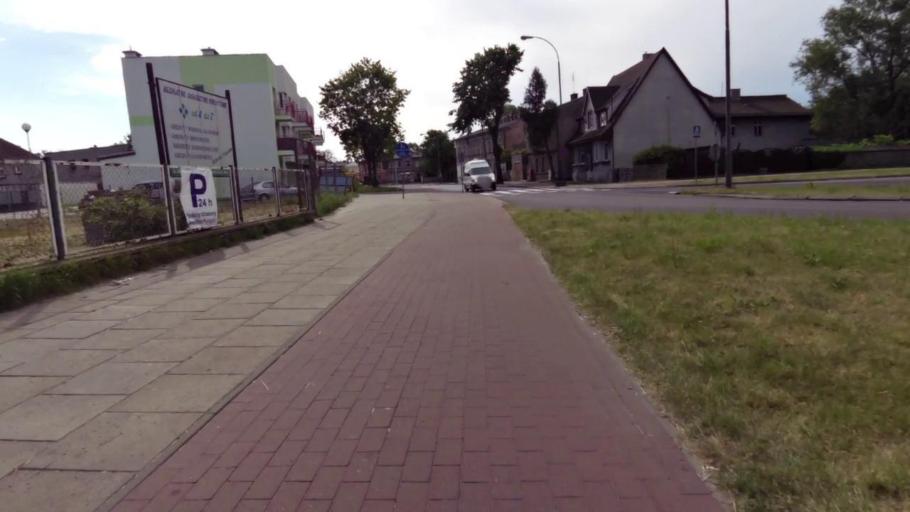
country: PL
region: West Pomeranian Voivodeship
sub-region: Swinoujscie
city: Swinoujscie
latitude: 53.9046
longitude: 14.2709
